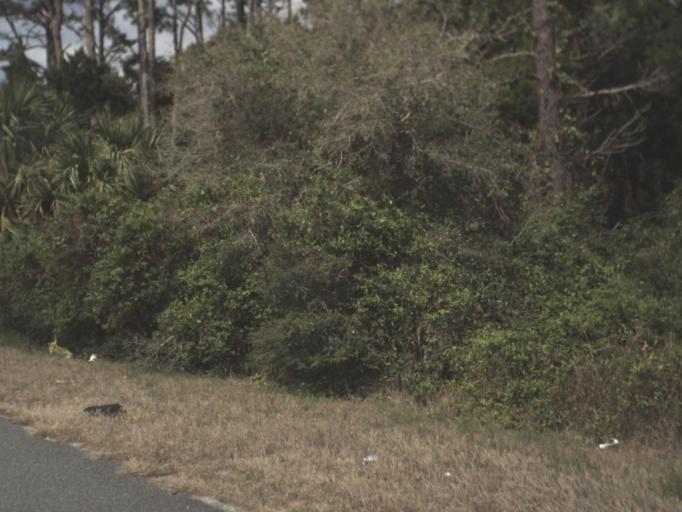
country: US
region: Florida
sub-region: Franklin County
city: Eastpoint
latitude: 29.7507
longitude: -84.8481
